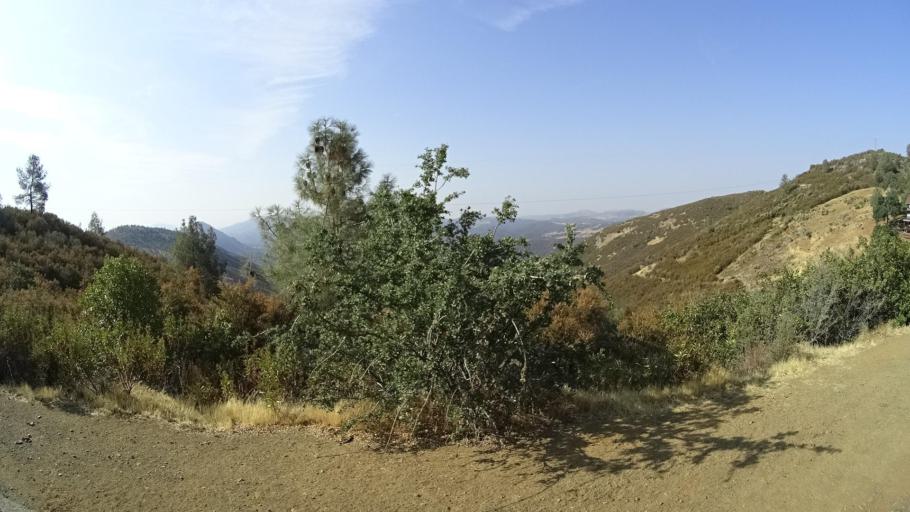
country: US
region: California
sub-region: Tuolumne County
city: Tuolumne City
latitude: 37.7272
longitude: -120.2481
